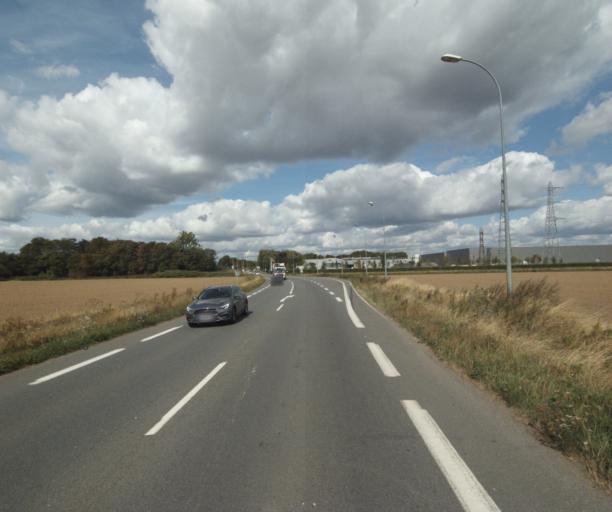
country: FR
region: Nord-Pas-de-Calais
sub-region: Departement du Nord
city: Sainghin-en-Melantois
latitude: 50.5939
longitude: 3.1505
